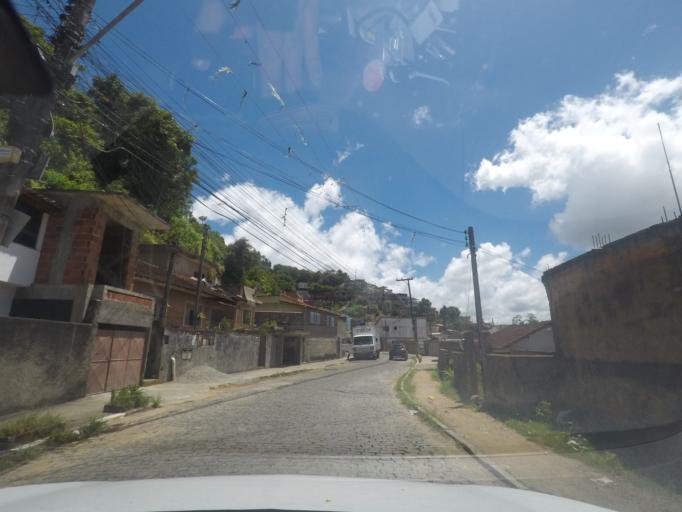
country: BR
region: Rio de Janeiro
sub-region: Teresopolis
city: Teresopolis
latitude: -22.4225
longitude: -42.9870
